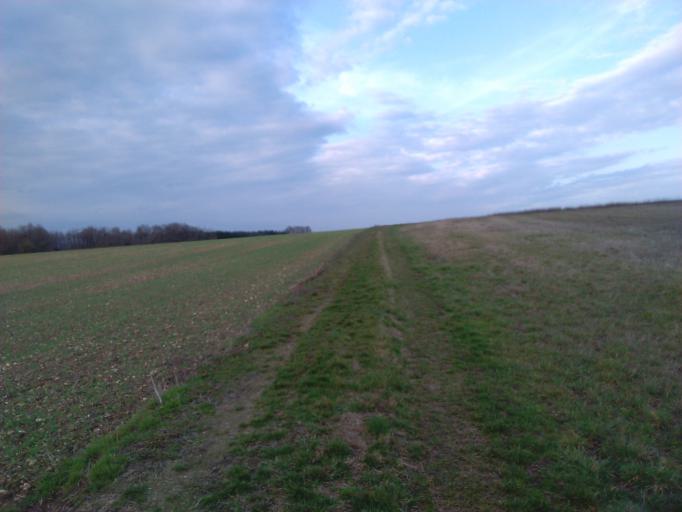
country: FR
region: Centre
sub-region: Departement du Loir-et-Cher
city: Villiers-sur-Loir
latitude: 47.8153
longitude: 0.9765
